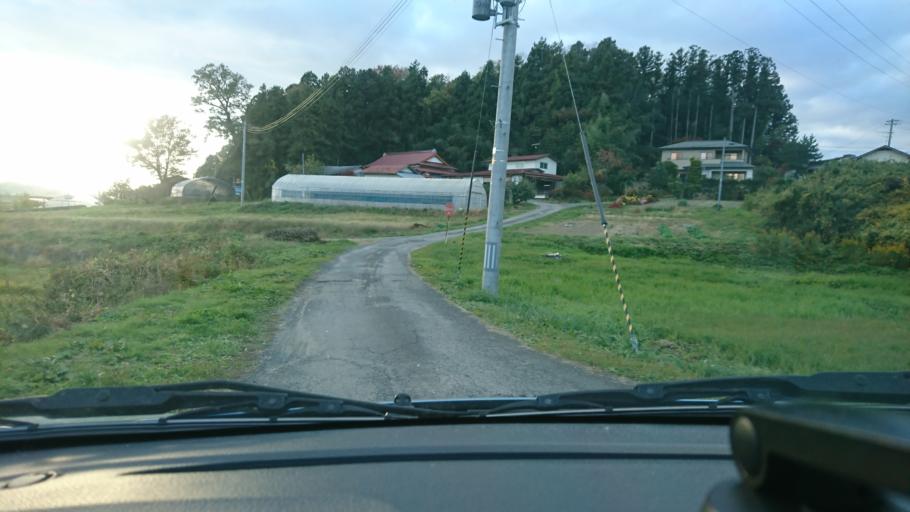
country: JP
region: Iwate
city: Ichinoseki
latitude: 38.7791
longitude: 141.2159
